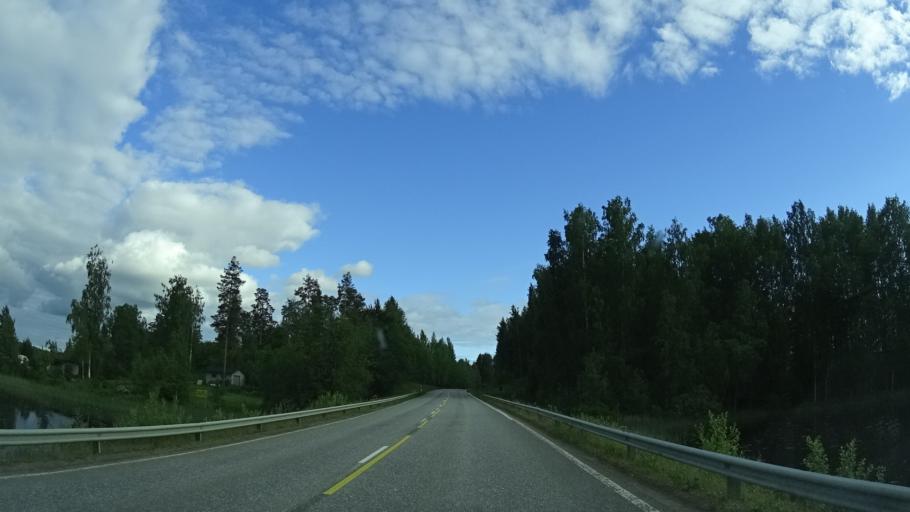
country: FI
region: Paijanne Tavastia
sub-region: Lahti
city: Sysmae
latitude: 61.4197
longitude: 25.6773
